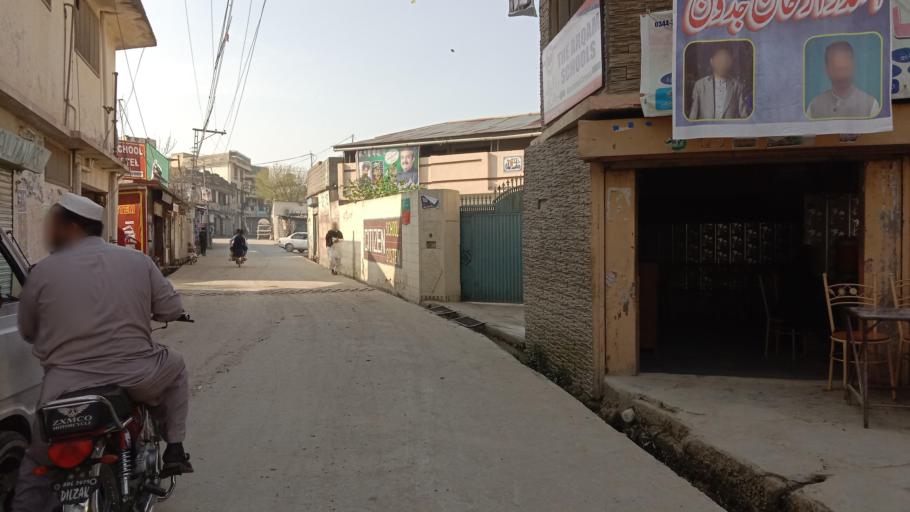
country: PK
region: Khyber Pakhtunkhwa
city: Abbottabad
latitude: 34.1979
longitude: 73.2294
